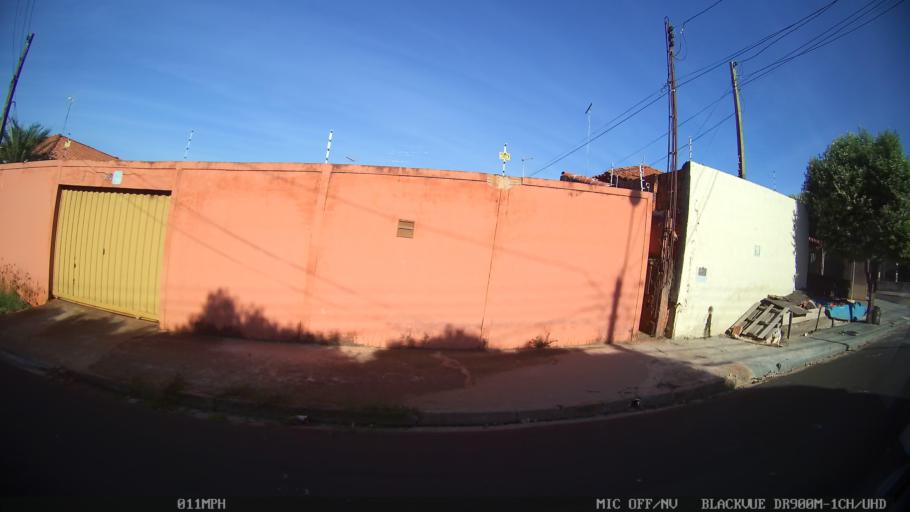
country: BR
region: Sao Paulo
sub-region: Sao Jose Do Rio Preto
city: Sao Jose do Rio Preto
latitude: -20.7812
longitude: -49.3623
